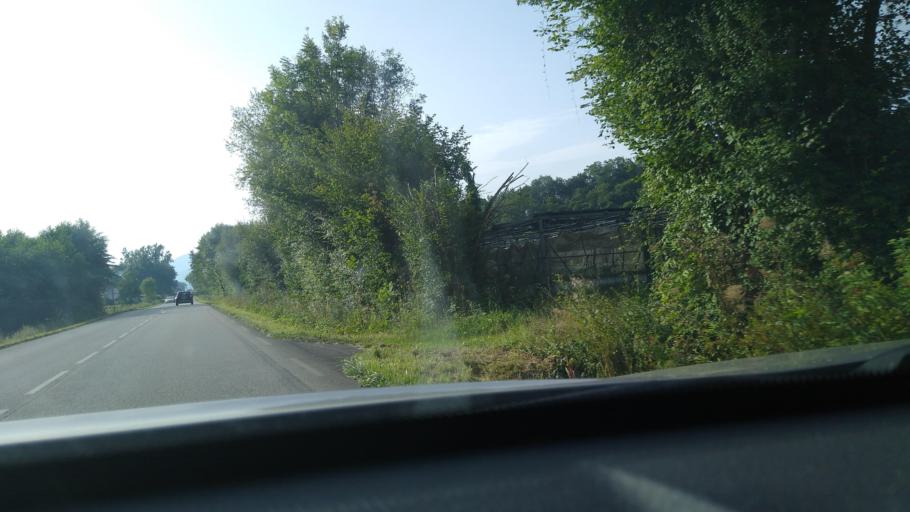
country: FR
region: Midi-Pyrenees
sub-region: Departement de l'Ariege
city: Saint-Lizier
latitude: 43.0260
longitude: 1.0903
